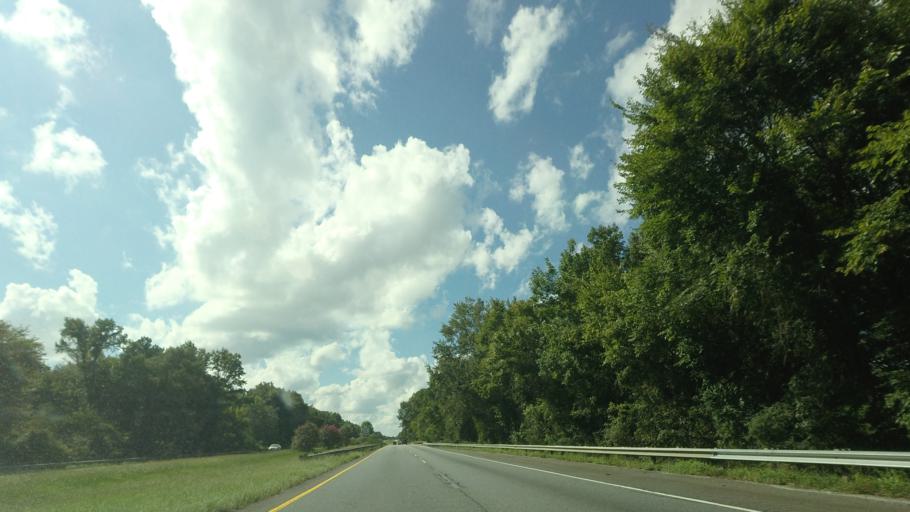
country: US
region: Georgia
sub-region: Bibb County
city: Macon
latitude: 32.8186
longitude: -83.5872
